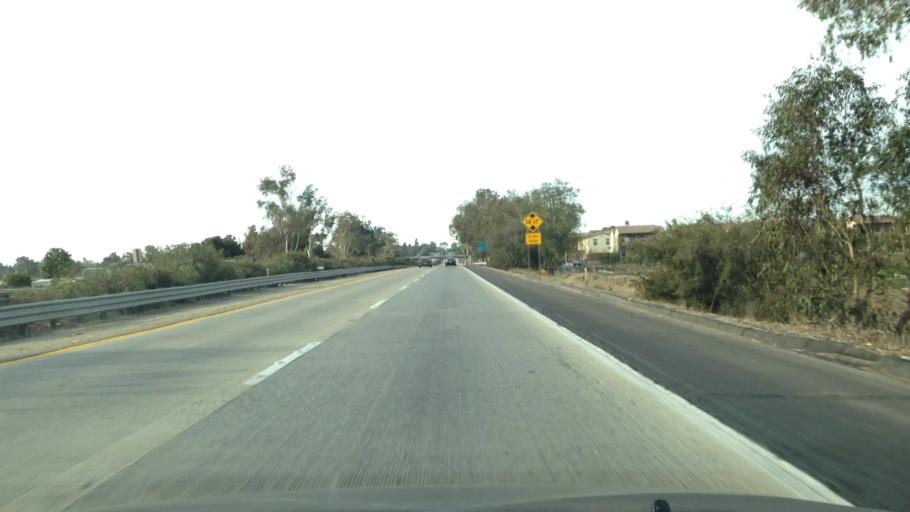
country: US
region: California
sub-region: Ventura County
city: Saticoy
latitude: 34.2947
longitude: -119.1481
